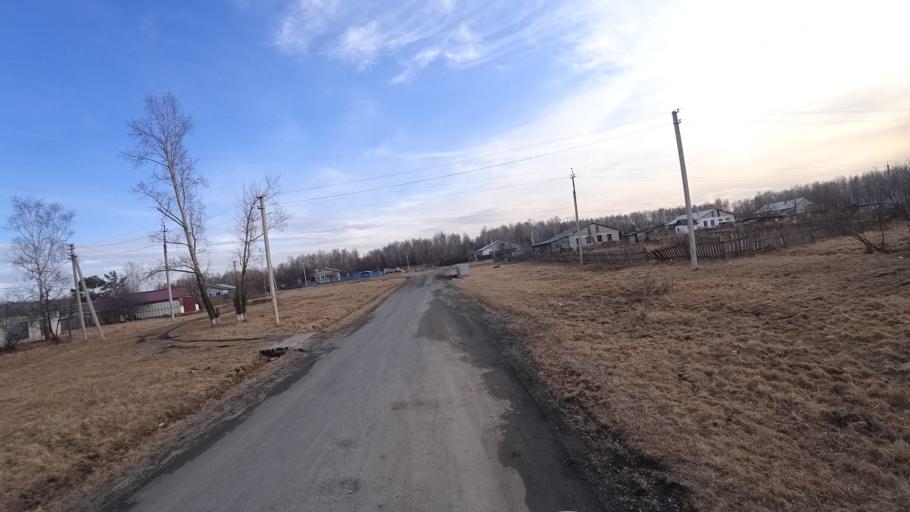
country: RU
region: Amur
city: Bureya
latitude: 50.0165
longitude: 129.7679
